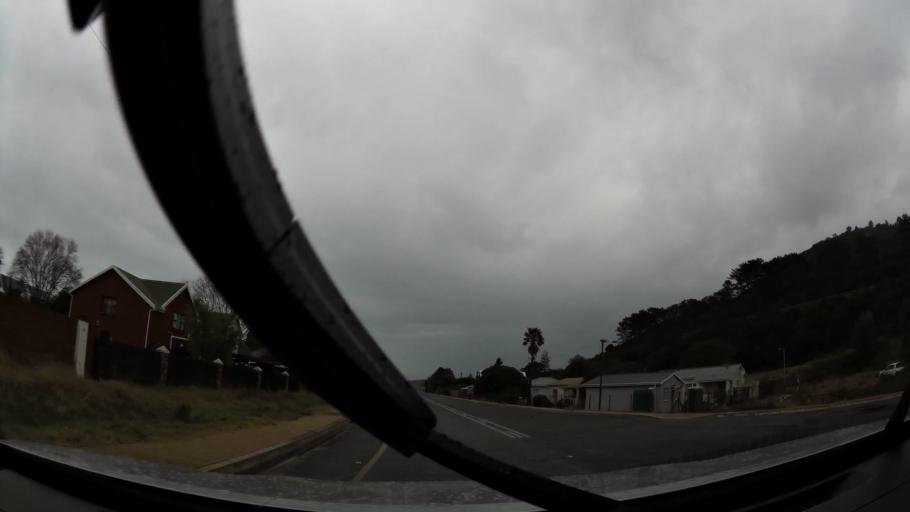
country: ZA
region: Western Cape
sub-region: Eden District Municipality
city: Mossel Bay
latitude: -34.0495
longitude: 22.2386
